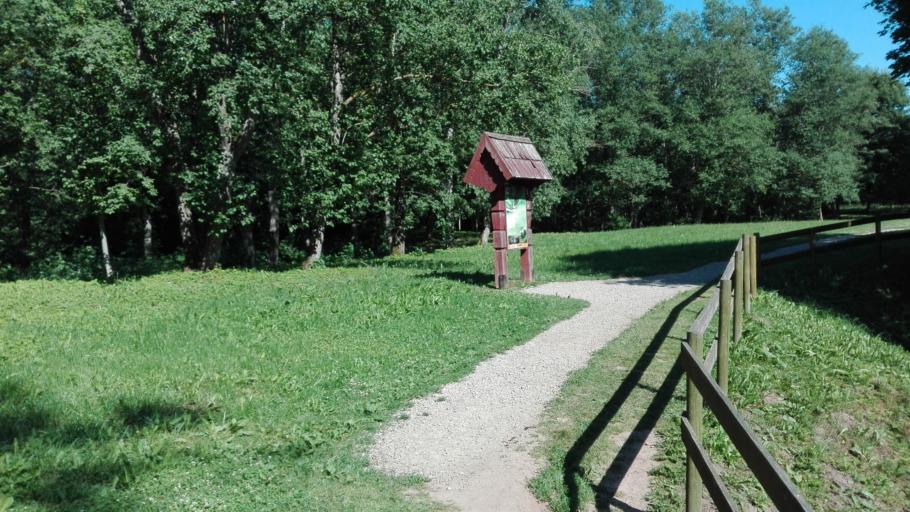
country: LT
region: Panevezys
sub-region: Birzai
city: Birzai
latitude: 56.2061
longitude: 24.6954
